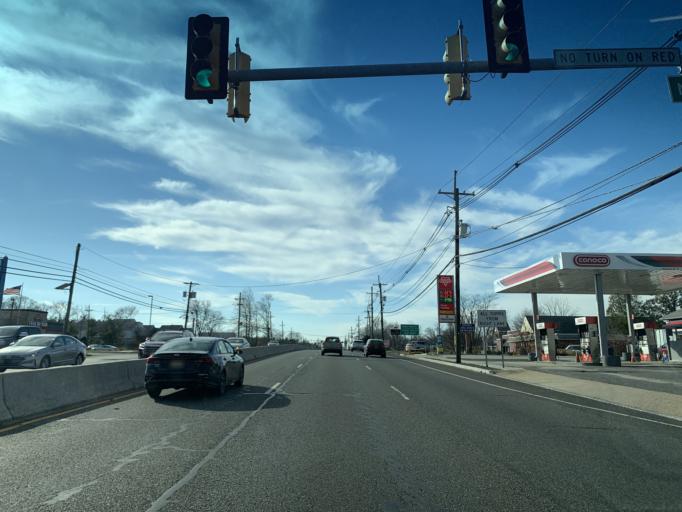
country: US
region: New Jersey
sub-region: Burlington County
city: Cinnaminson
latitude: 40.0126
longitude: -74.9612
